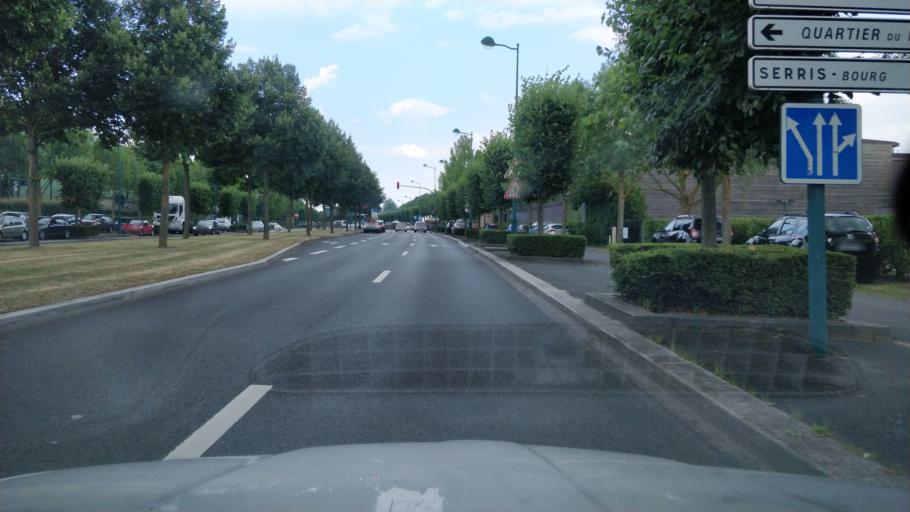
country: FR
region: Ile-de-France
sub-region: Departement de Seine-et-Marne
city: Serris
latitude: 48.8511
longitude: 2.7849
